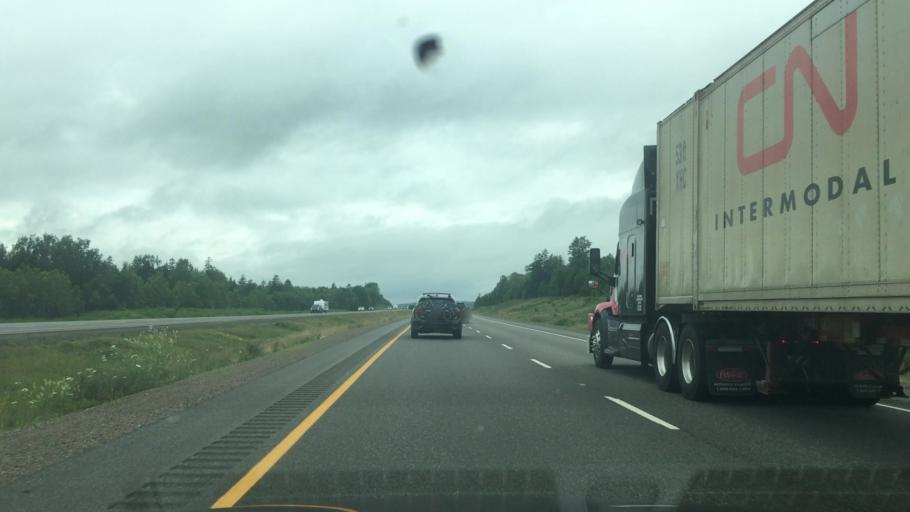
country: CA
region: Nova Scotia
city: Truro
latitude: 45.4483
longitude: -63.6118
